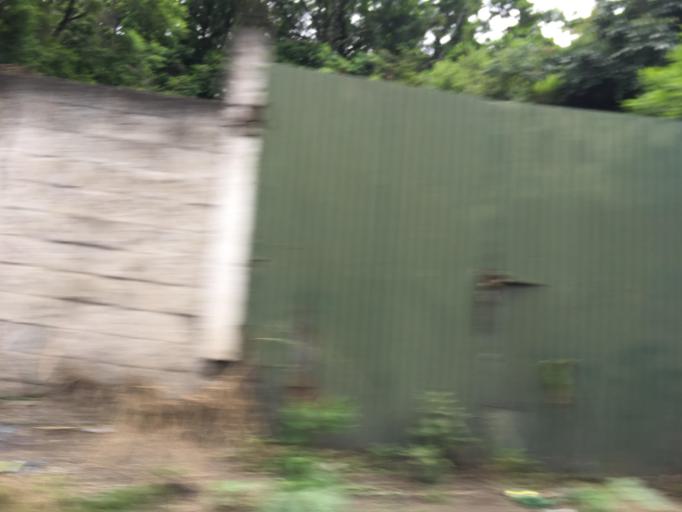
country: GT
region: Guatemala
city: Amatitlan
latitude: 14.4613
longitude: -90.5805
